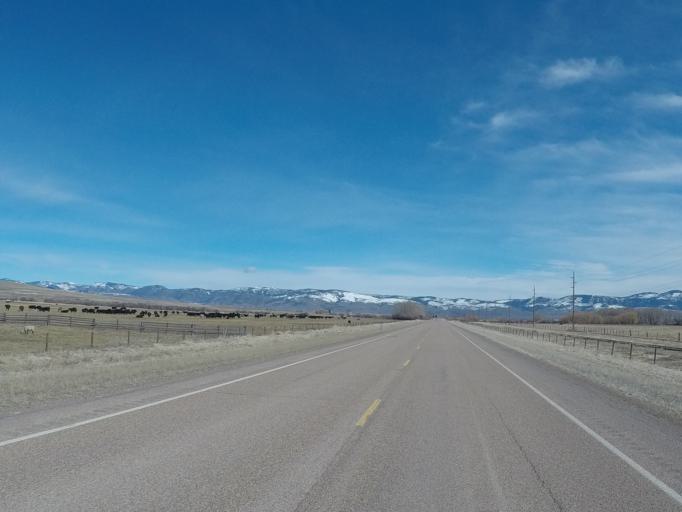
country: US
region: Montana
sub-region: Granite County
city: Philipsburg
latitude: 46.5572
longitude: -113.2157
